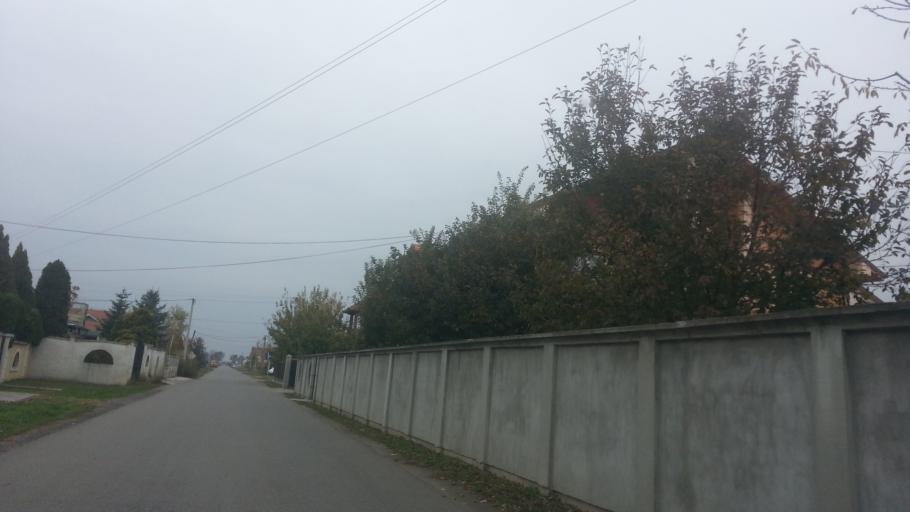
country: RS
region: Autonomna Pokrajina Vojvodina
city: Nova Pazova
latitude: 44.9523
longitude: 20.2086
